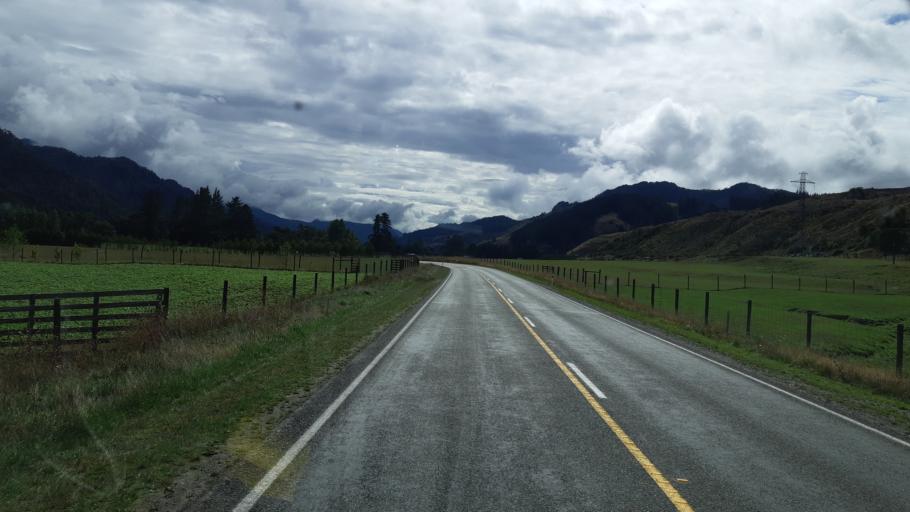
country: NZ
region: West Coast
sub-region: Buller District
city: Westport
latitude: -41.7785
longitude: 172.3760
